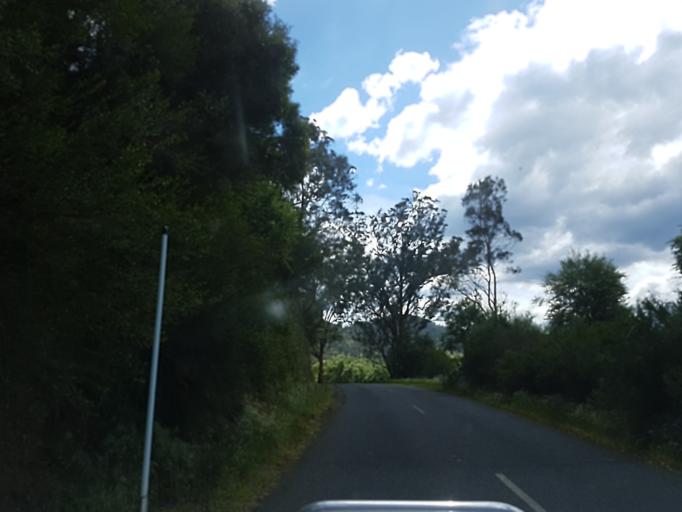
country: AU
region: Victoria
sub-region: East Gippsland
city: Bairnsdale
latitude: -37.4442
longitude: 147.2489
